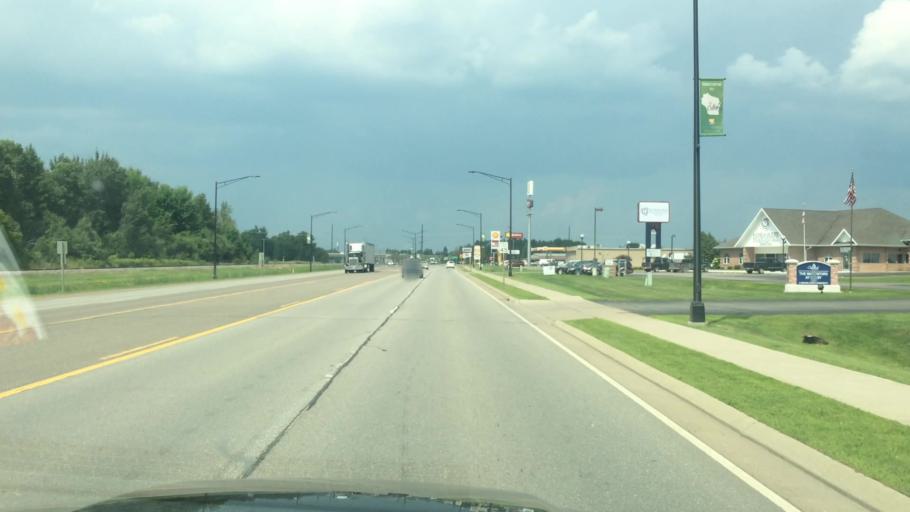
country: US
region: Wisconsin
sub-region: Clark County
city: Colby
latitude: 44.9262
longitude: -90.3154
